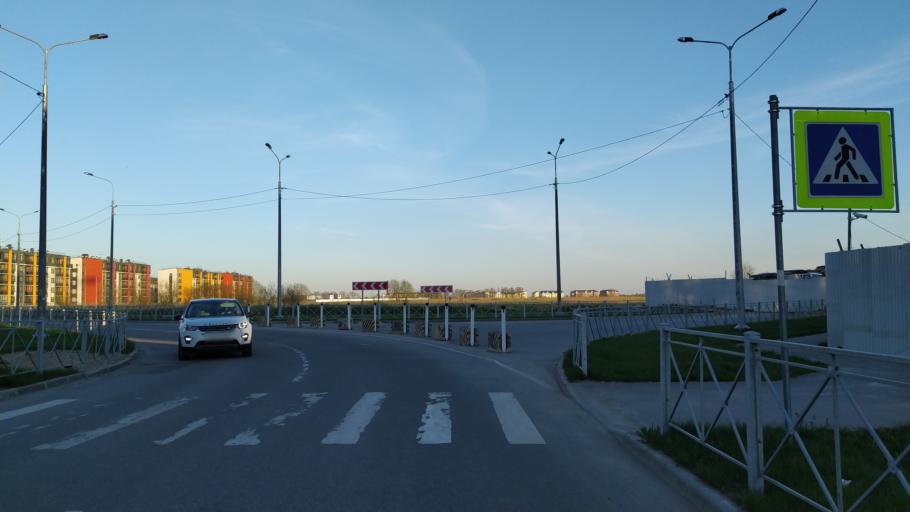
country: RU
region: St.-Petersburg
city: Pushkin
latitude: 59.6994
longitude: 30.4019
